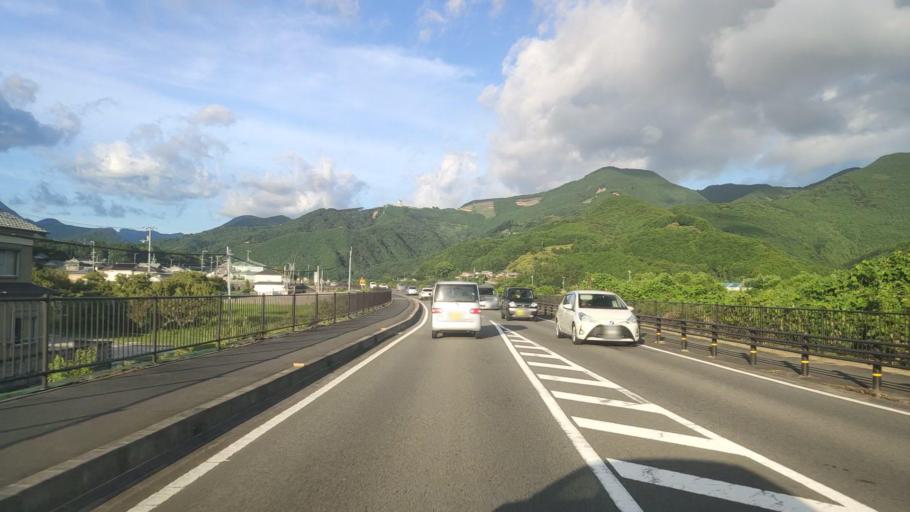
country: JP
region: Wakayama
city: Tanabe
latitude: 33.7159
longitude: 135.4682
